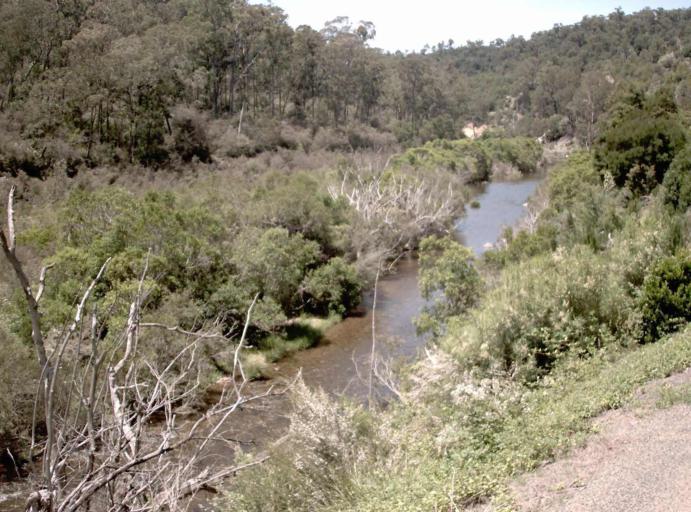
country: AU
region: Victoria
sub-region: East Gippsland
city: Lakes Entrance
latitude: -37.5527
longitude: 147.8771
